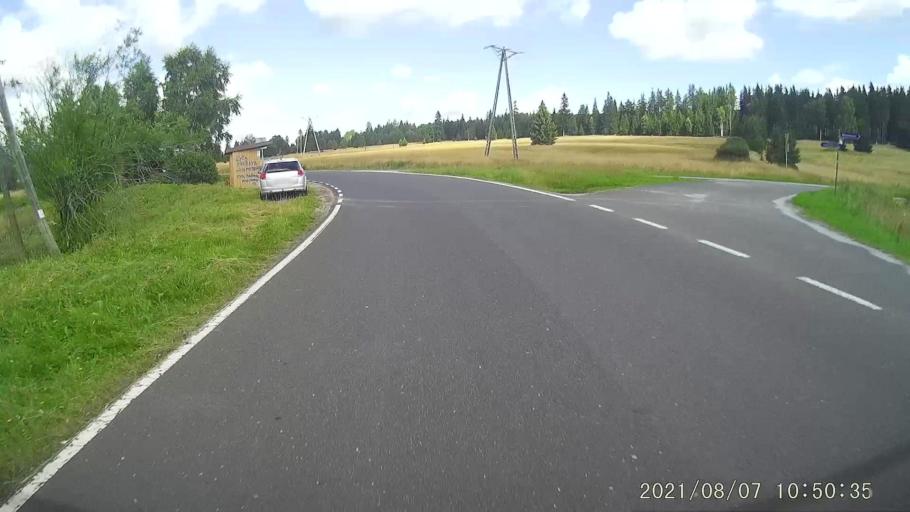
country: PL
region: Lower Silesian Voivodeship
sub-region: Powiat klodzki
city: Polanica-Zdroj
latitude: 50.2964
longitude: 16.4654
